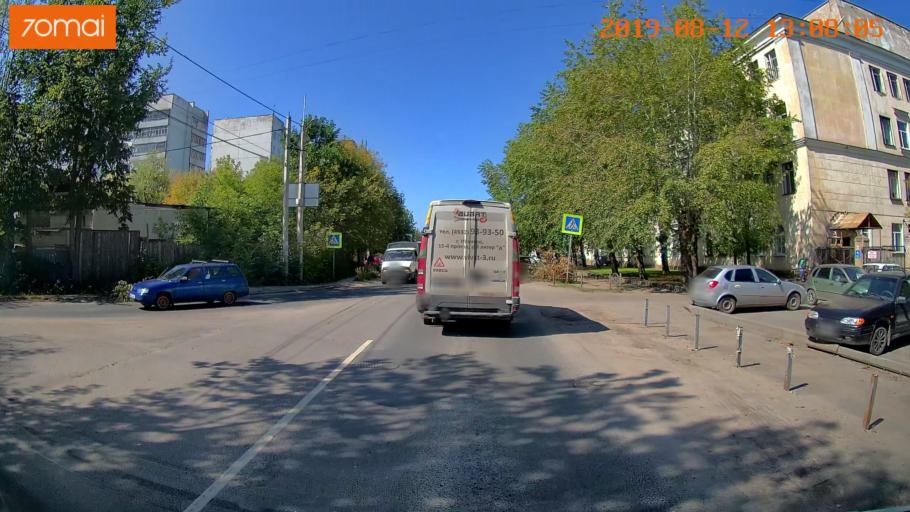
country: RU
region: Ivanovo
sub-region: Gorod Ivanovo
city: Ivanovo
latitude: 57.0078
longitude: 40.9992
